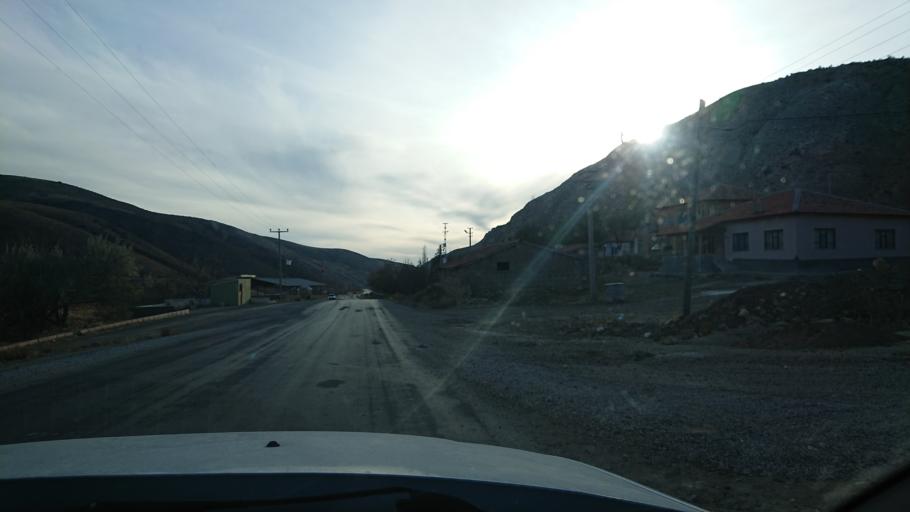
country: TR
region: Ankara
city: Sereflikochisar
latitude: 38.7619
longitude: 33.6977
